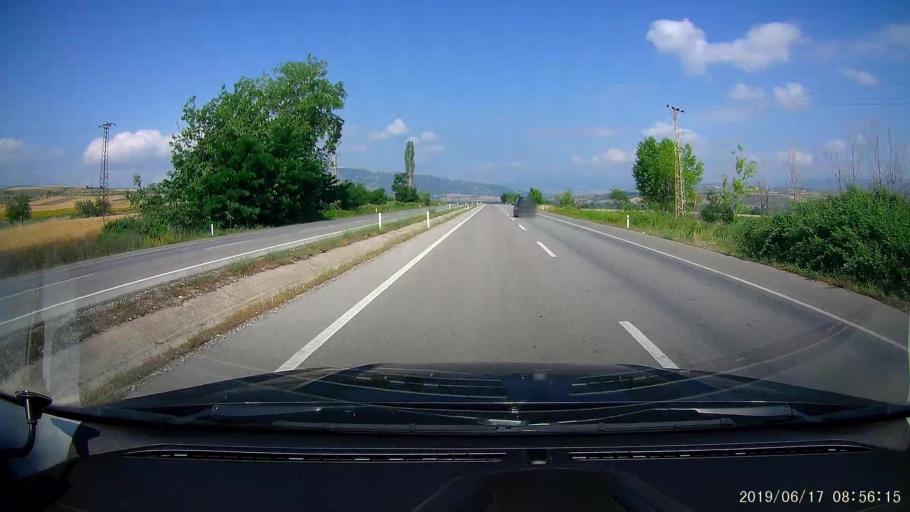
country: TR
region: Amasya
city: Esencay
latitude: 40.7336
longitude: 36.4258
